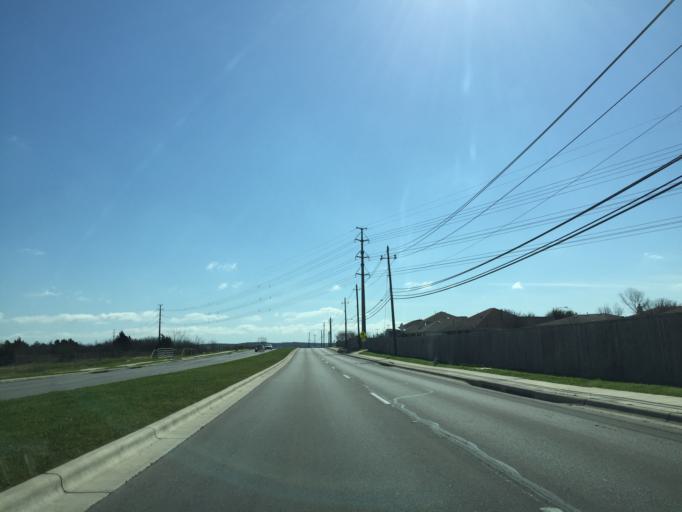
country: US
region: Texas
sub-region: Travis County
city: Garfield
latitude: 30.1599
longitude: -97.6463
